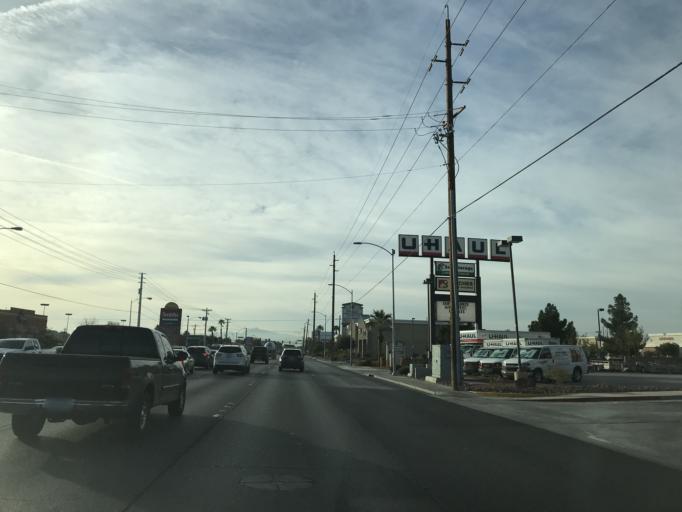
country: US
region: Nevada
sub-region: Clark County
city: Sunrise Manor
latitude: 36.1690
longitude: -115.0622
